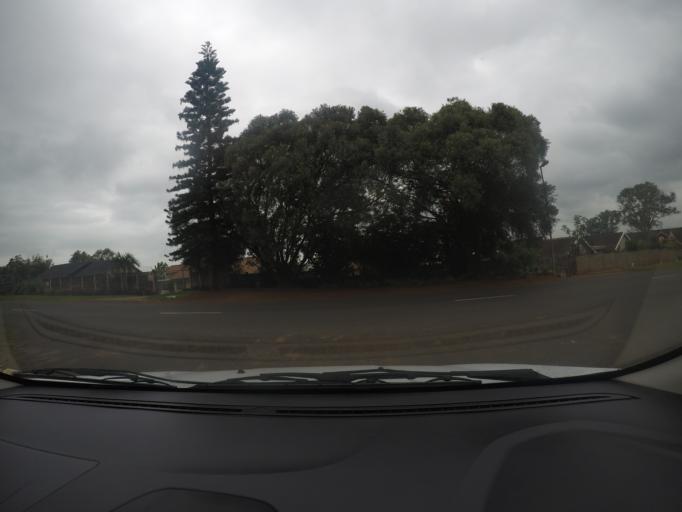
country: ZA
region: KwaZulu-Natal
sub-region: uThungulu District Municipality
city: Empangeni
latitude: -28.7692
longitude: 31.8962
